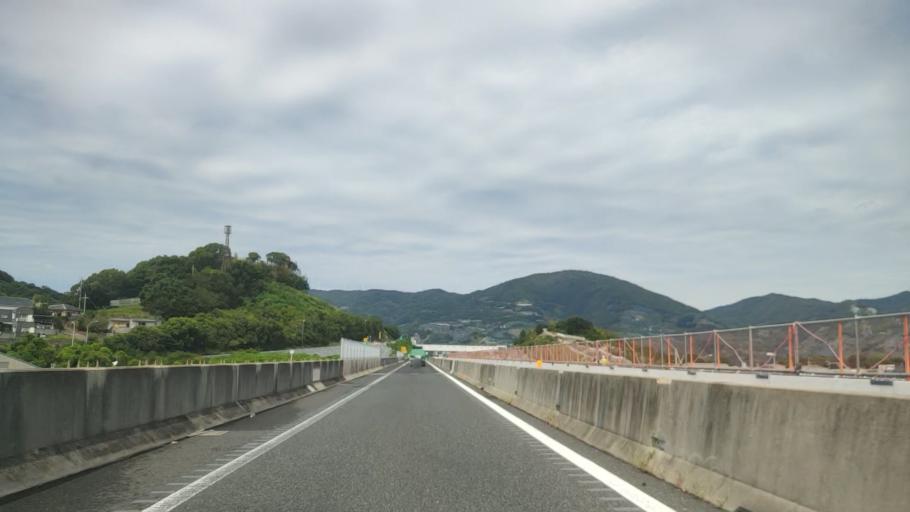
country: JP
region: Wakayama
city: Kainan
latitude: 34.0570
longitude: 135.2007
